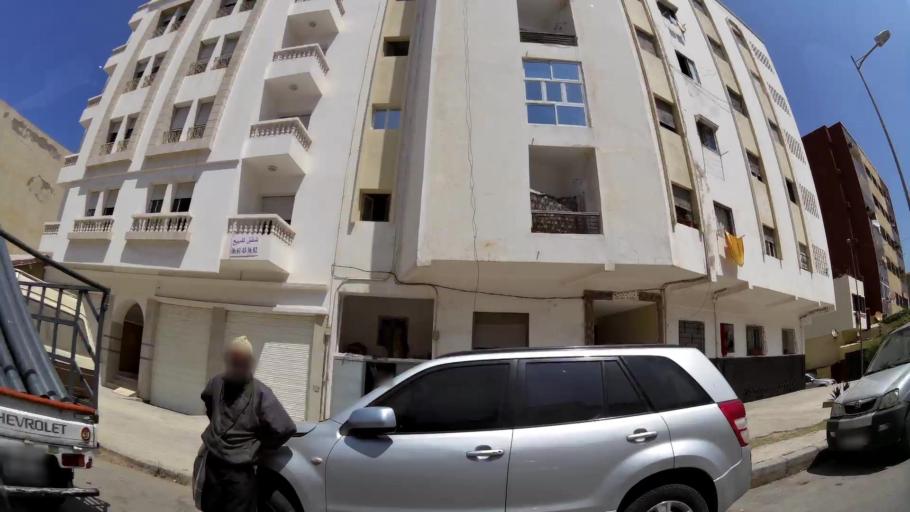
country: MA
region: Rabat-Sale-Zemmour-Zaer
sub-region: Rabat
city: Rabat
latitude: 34.0261
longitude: -6.8479
